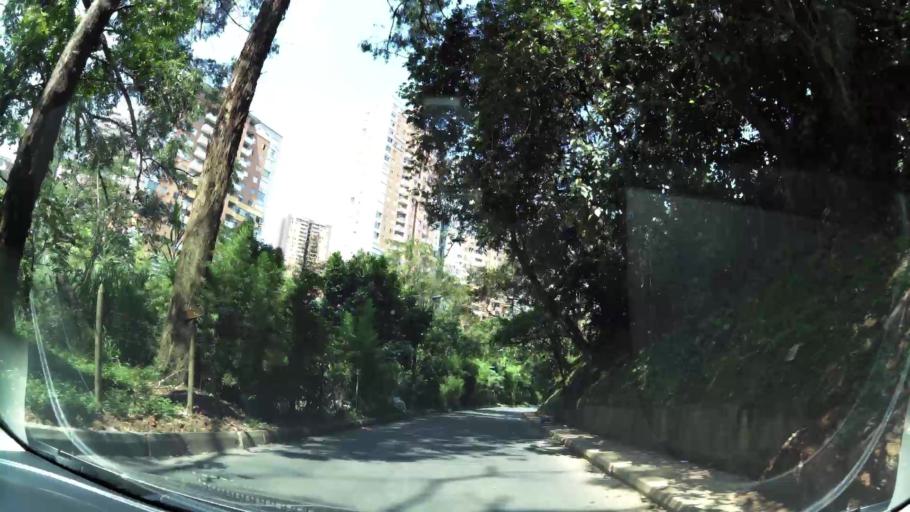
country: CO
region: Antioquia
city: Itagui
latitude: 6.2163
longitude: -75.6043
